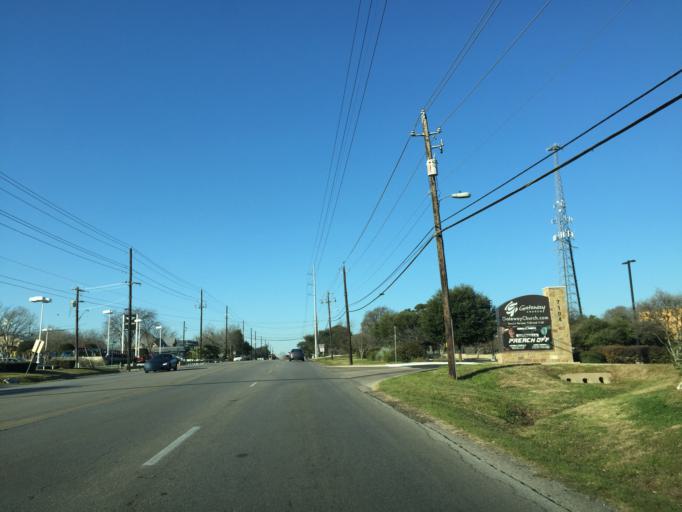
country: US
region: Texas
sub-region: Williamson County
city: Jollyville
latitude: 30.4367
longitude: -97.7627
